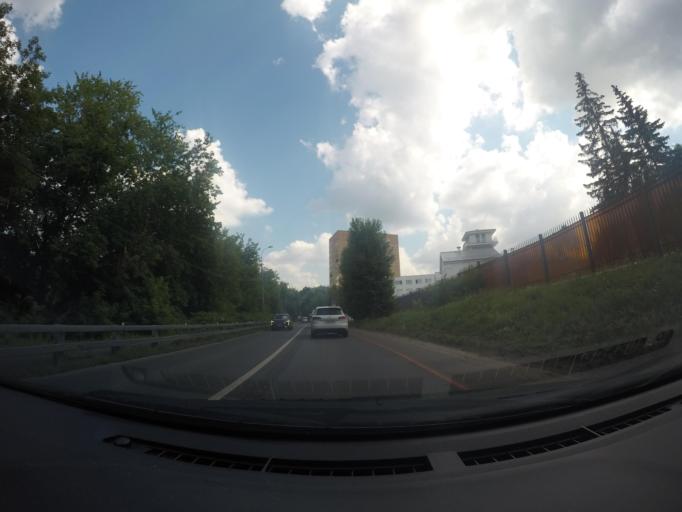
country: RU
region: Moscow
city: Sviblovo
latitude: 55.8393
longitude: 37.6303
